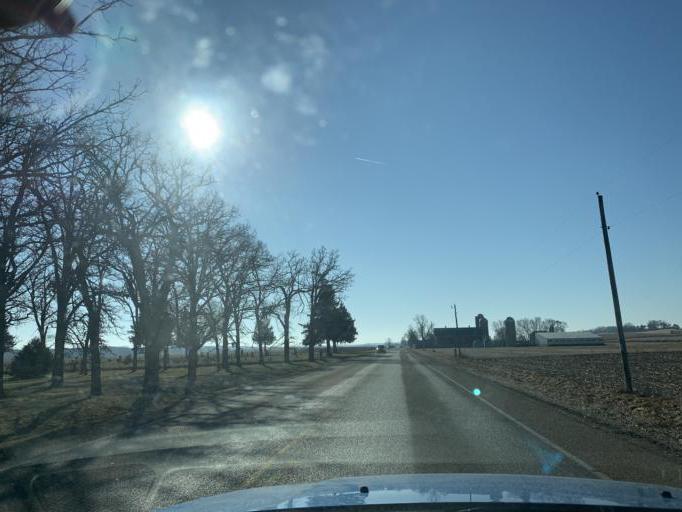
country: US
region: Wisconsin
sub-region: Dane County
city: Belleville
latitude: 42.9230
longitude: -89.5303
